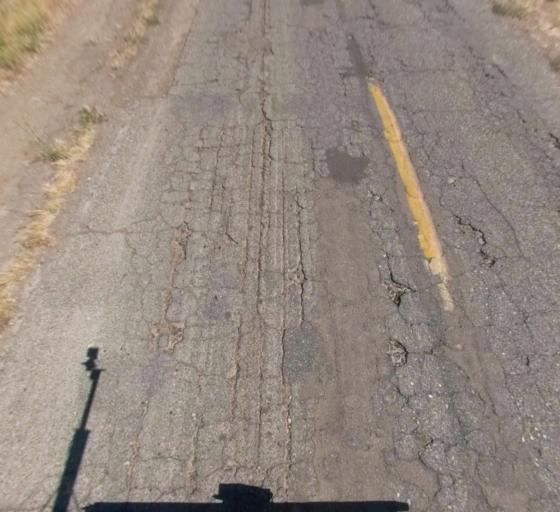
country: US
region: California
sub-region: Madera County
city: Parkwood
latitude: 36.8796
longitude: -120.0195
